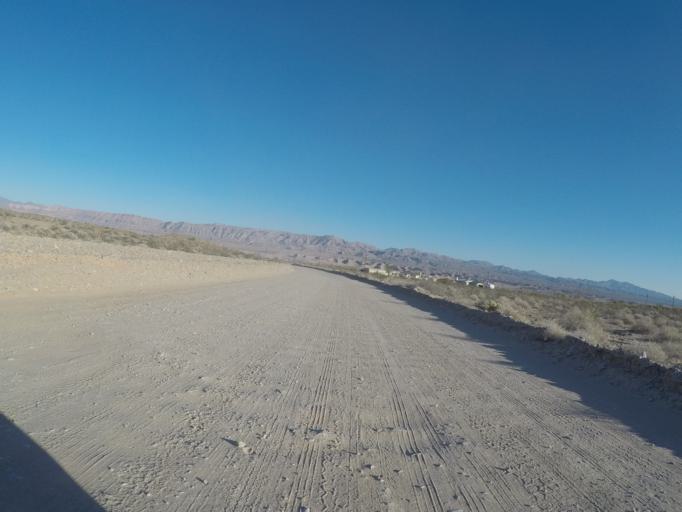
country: US
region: Nevada
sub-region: Clark County
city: Moapa Valley
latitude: 36.3857
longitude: -114.4124
